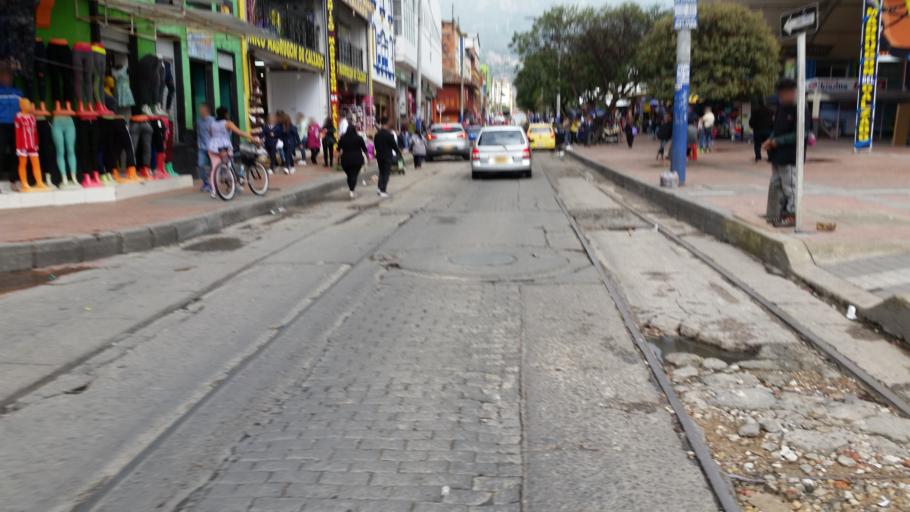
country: CO
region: Bogota D.C.
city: Bogota
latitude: 4.6006
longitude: -74.0809
